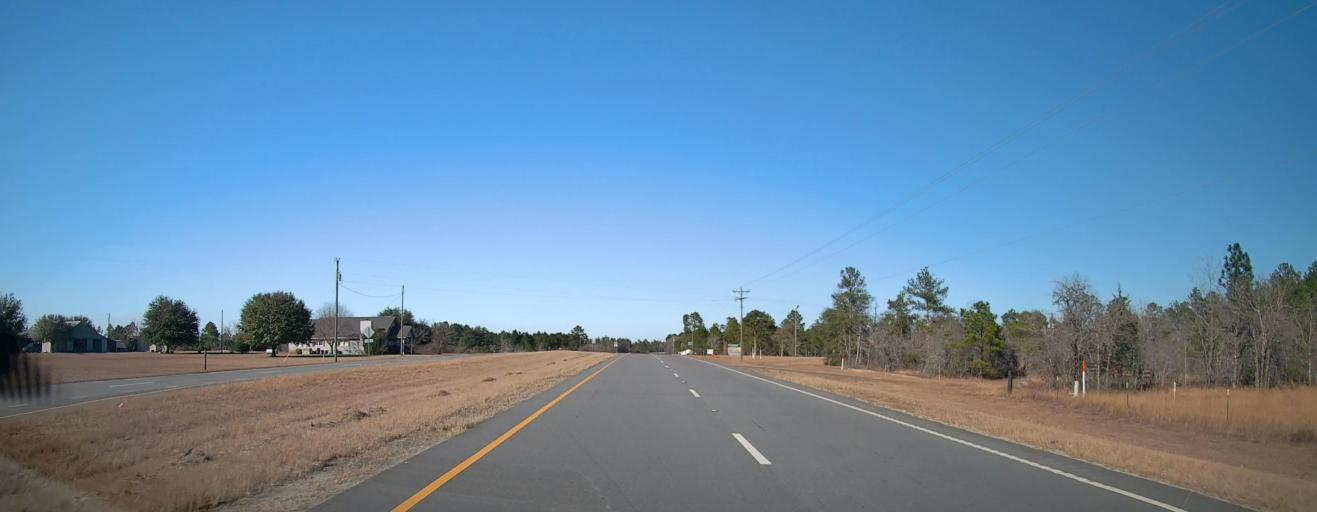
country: US
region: Georgia
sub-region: Taylor County
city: Butler
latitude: 32.5983
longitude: -84.2392
